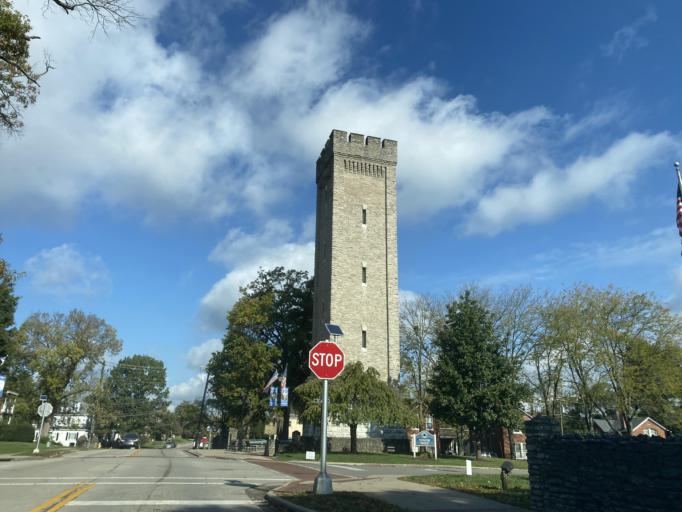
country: US
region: Kentucky
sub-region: Campbell County
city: Fort Thomas
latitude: 39.0671
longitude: -84.4469
